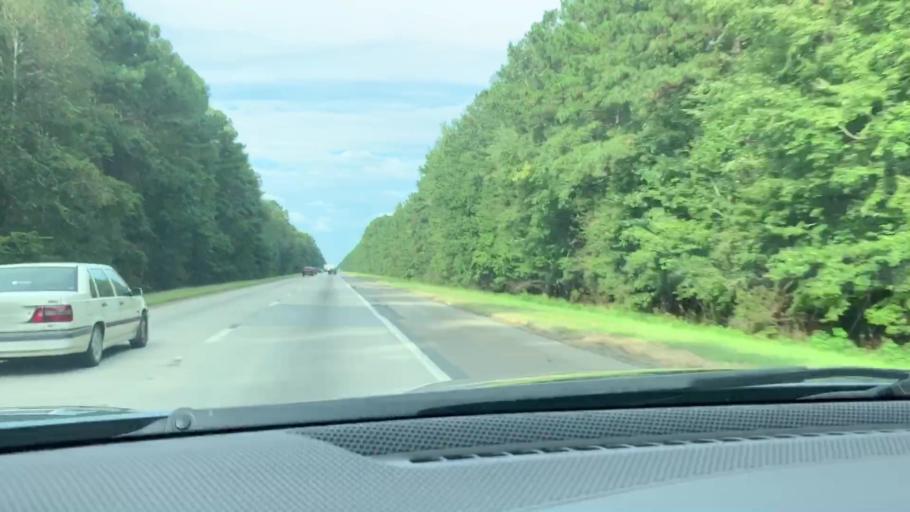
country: US
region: South Carolina
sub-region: Colleton County
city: Walterboro
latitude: 32.9731
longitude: -80.6754
